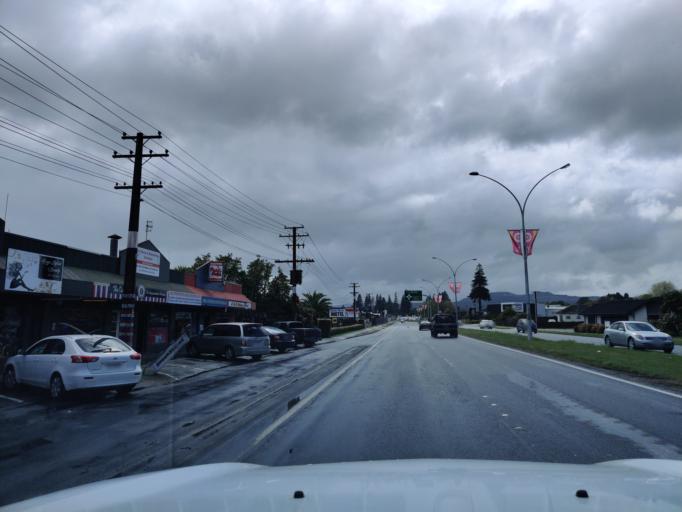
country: NZ
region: Bay of Plenty
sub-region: Rotorua District
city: Rotorua
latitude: -38.1488
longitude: 176.2735
